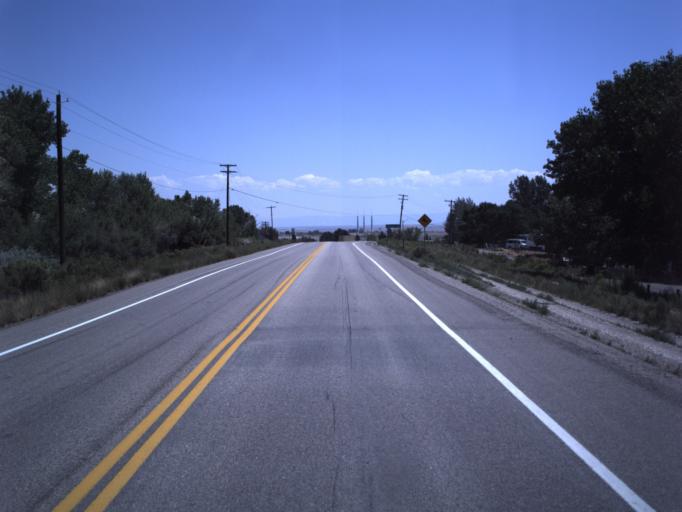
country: US
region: Utah
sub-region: Emery County
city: Ferron
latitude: 39.1264
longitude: -111.1066
